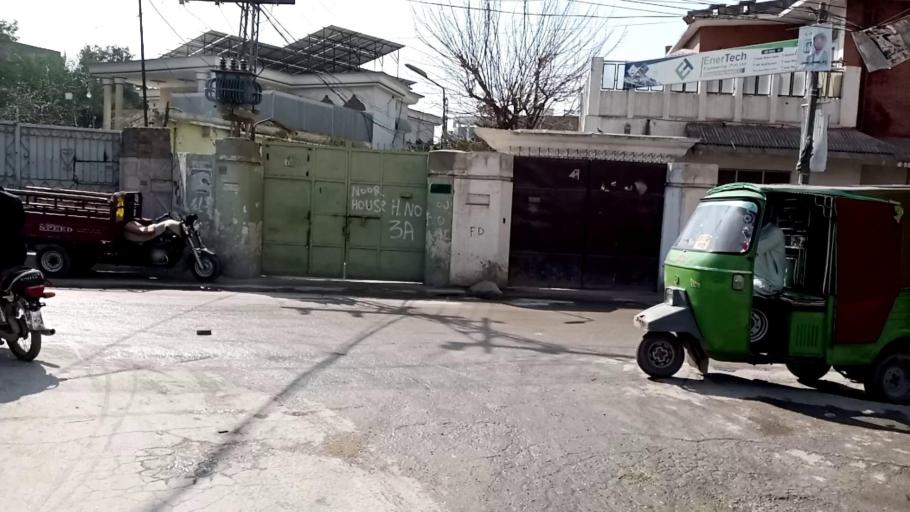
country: PK
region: Khyber Pakhtunkhwa
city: Peshawar
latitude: 34.0095
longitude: 71.5107
